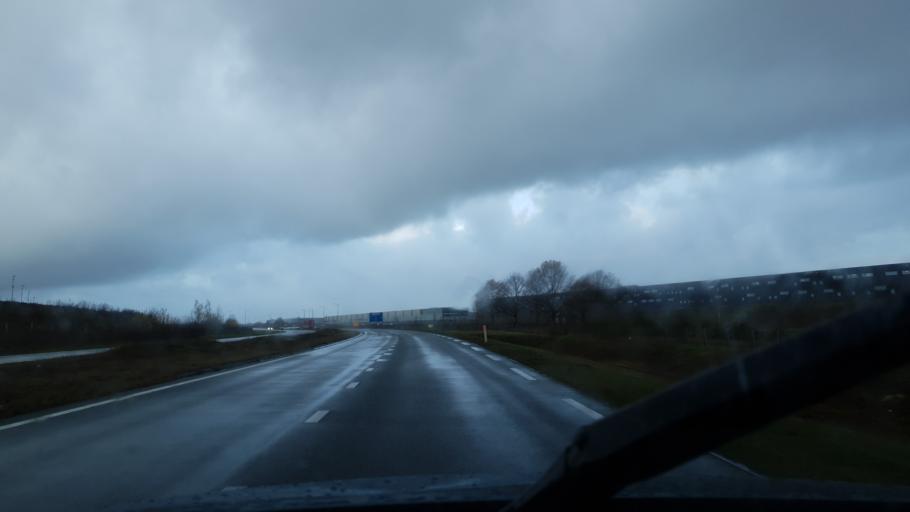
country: NL
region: Limburg
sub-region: Gemeente Venlo
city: Tegelen
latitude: 51.4125
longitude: 6.1028
